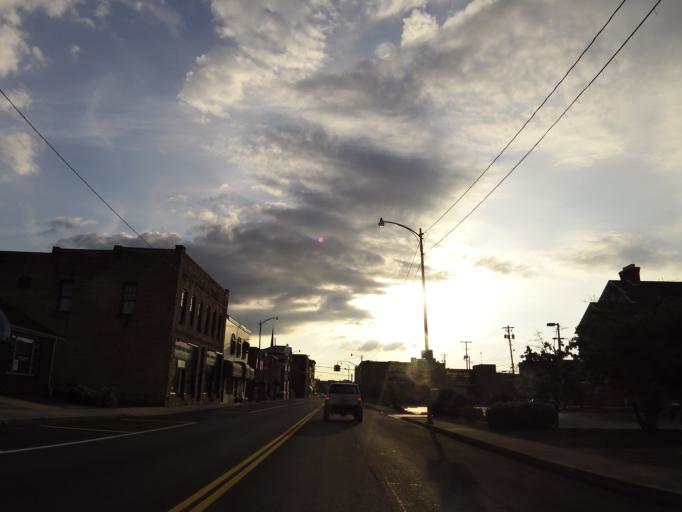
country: US
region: Tennessee
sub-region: Cocke County
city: Newport
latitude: 35.9667
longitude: -83.1853
